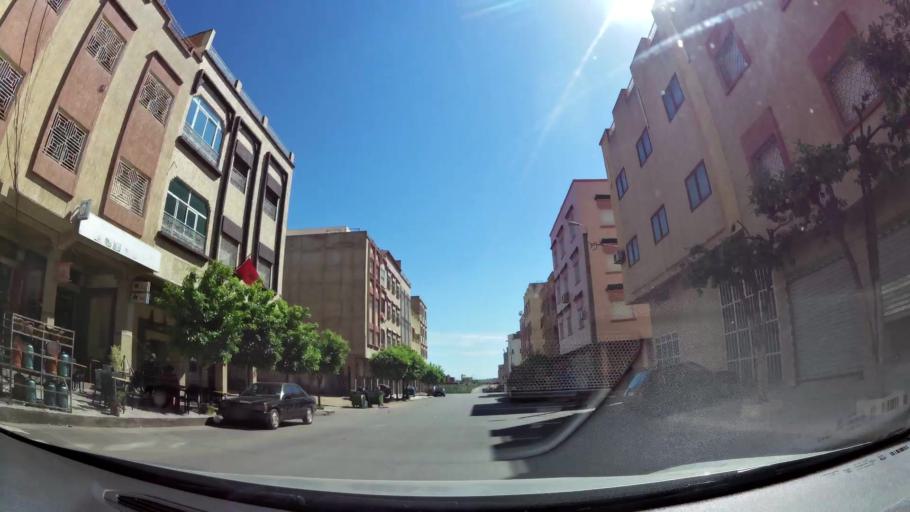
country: MA
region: Meknes-Tafilalet
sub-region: Meknes
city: Meknes
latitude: 33.8854
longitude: -5.5793
